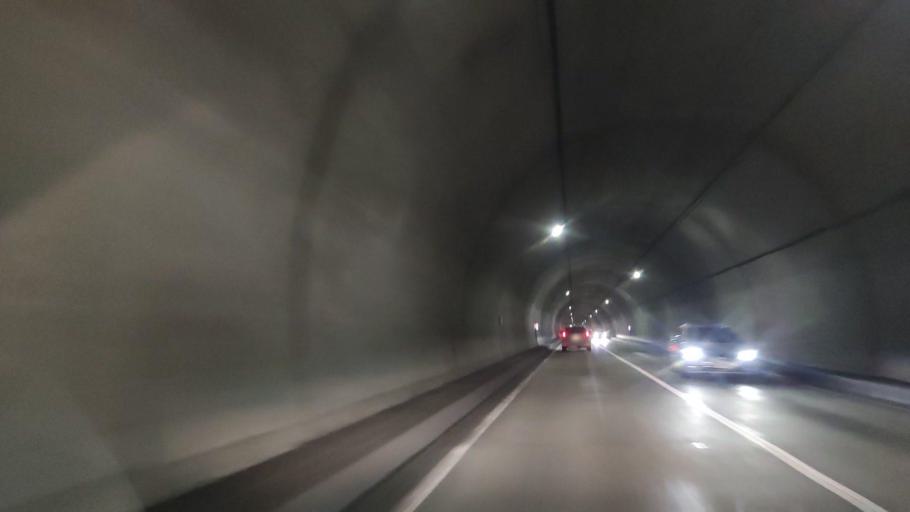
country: JP
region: Hokkaido
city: Ishikari
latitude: 43.5321
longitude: 141.3934
